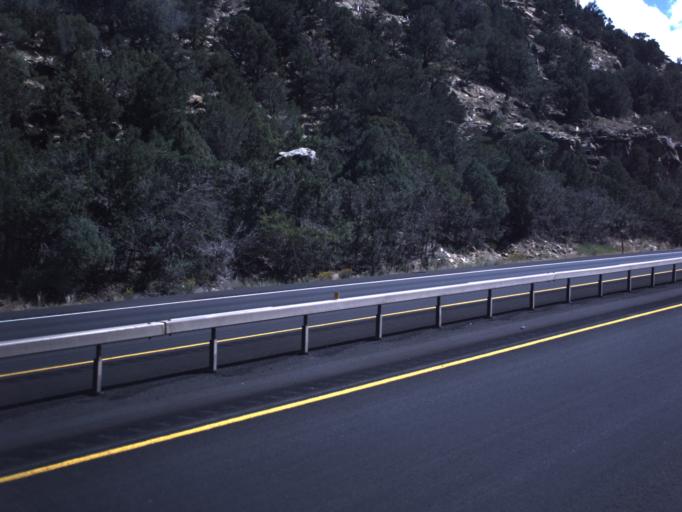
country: US
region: Utah
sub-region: Sevier County
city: Salina
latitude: 38.8856
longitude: -111.6047
